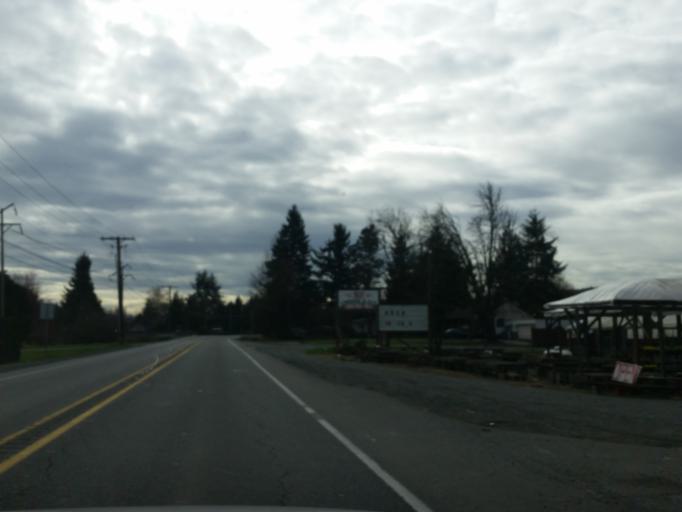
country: US
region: Washington
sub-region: Pierce County
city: Alderton
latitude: 47.1587
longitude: -122.2295
